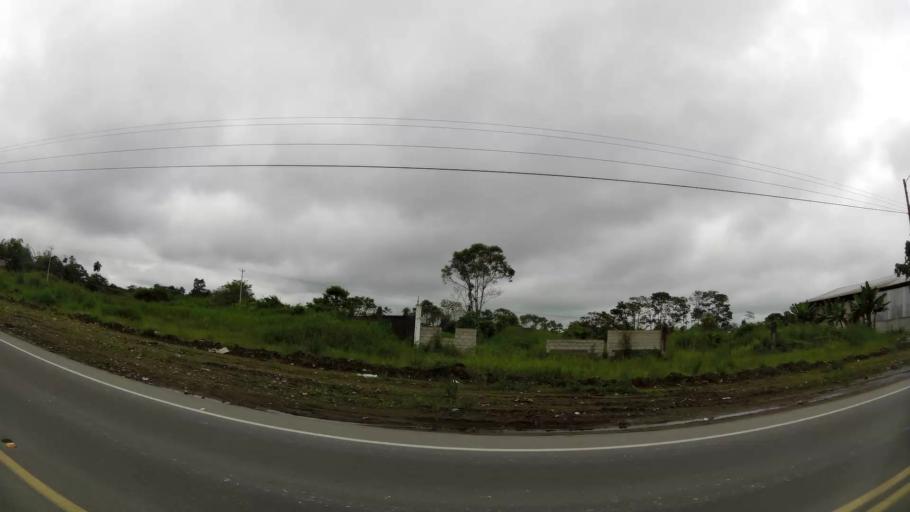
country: EC
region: Santo Domingo de los Tsachilas
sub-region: Canton Santo Domingo de los Colorados
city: Santo Domingo de los Colorados
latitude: -0.2772
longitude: -79.1958
